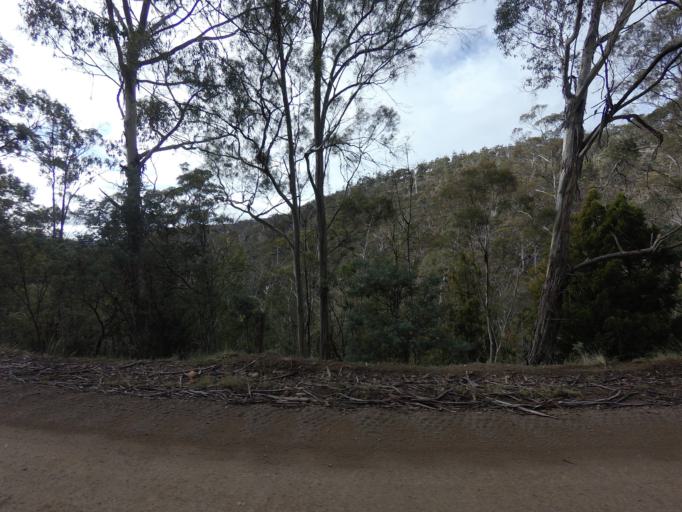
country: AU
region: Tasmania
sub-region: Derwent Valley
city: New Norfolk
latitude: -42.7435
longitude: 146.8671
